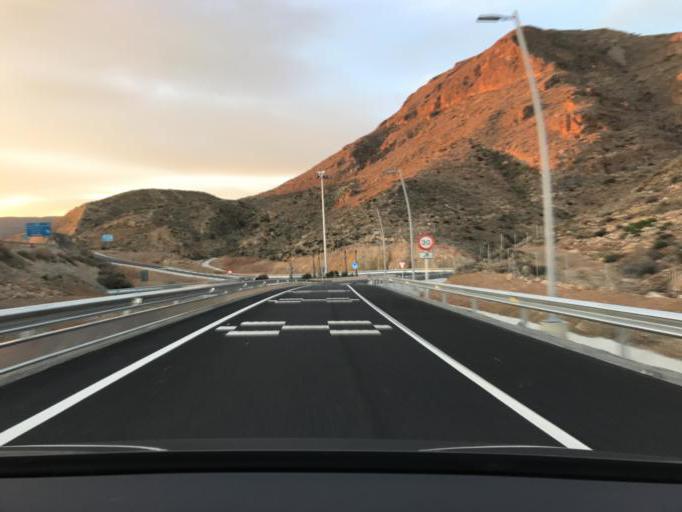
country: ES
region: Andalusia
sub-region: Provincia de Almeria
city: Aguadulce
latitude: 36.8263
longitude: -2.5815
